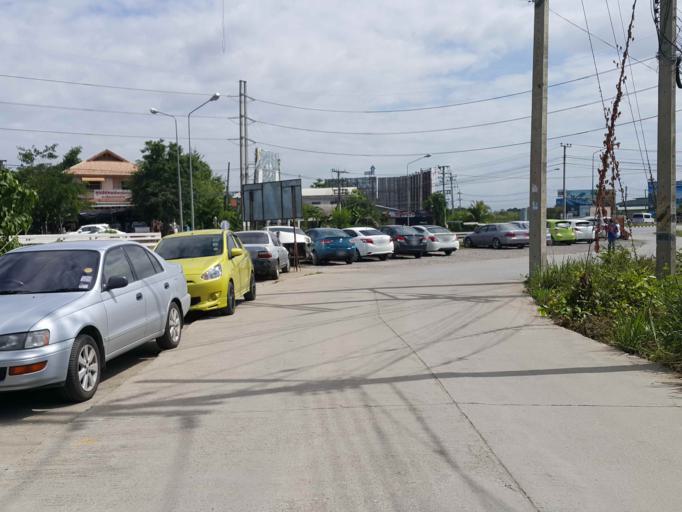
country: TH
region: Chiang Mai
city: Saraphi
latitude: 18.7516
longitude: 99.0569
